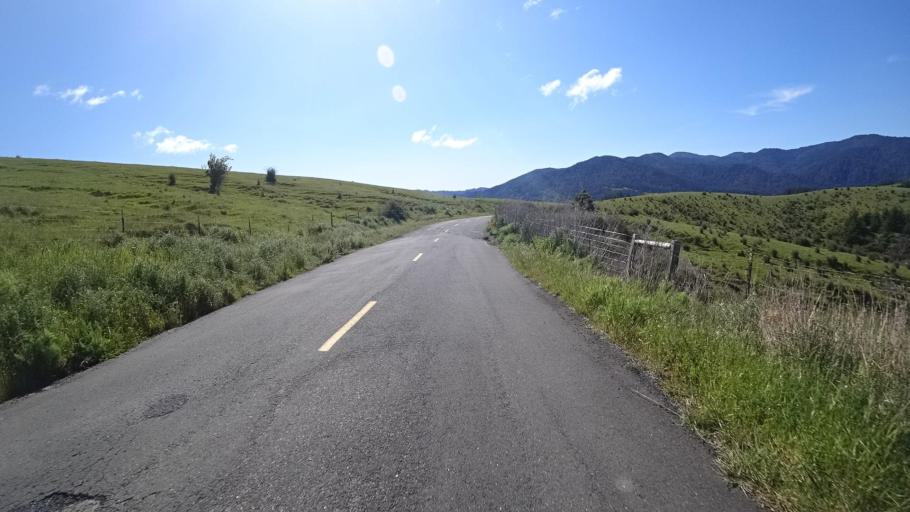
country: US
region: California
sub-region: Humboldt County
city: Ferndale
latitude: 40.3335
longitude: -124.3026
